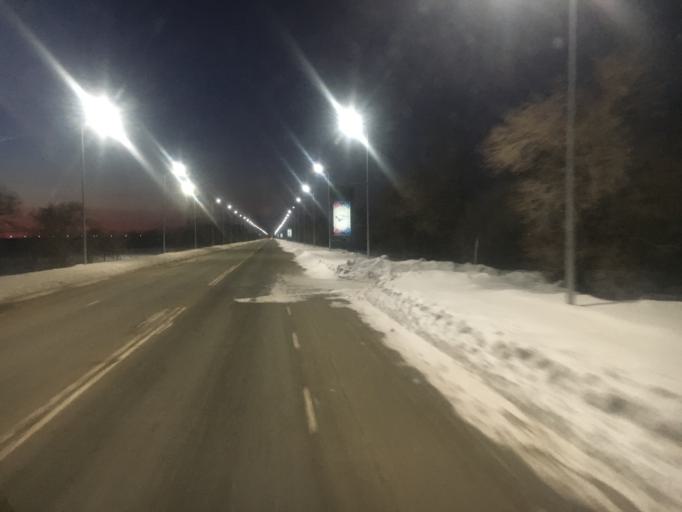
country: KZ
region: Batys Qazaqstan
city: Oral
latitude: 51.1551
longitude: 51.5368
